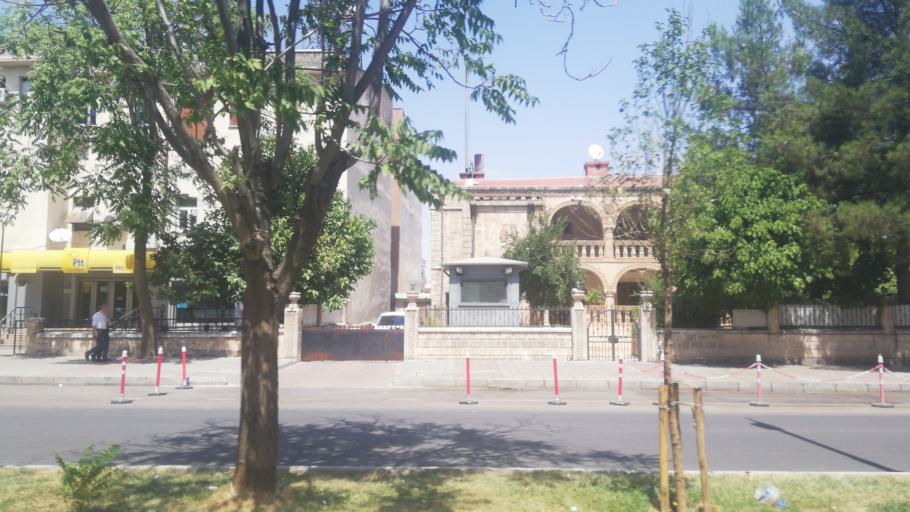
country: TR
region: Mardin
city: Midyat
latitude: 37.4240
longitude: 41.3419
